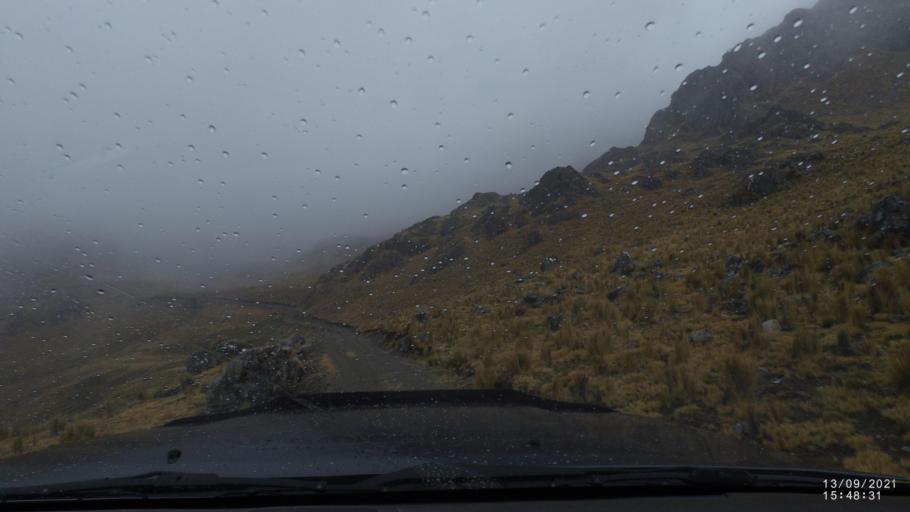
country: BO
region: Cochabamba
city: Colomi
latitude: -17.3106
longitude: -65.7158
